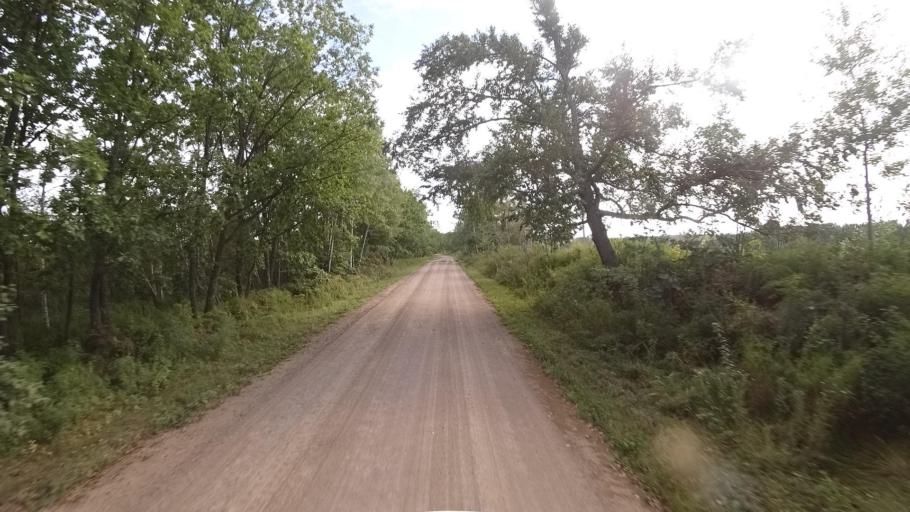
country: RU
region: Primorskiy
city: Dostoyevka
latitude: 44.3651
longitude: 133.5204
